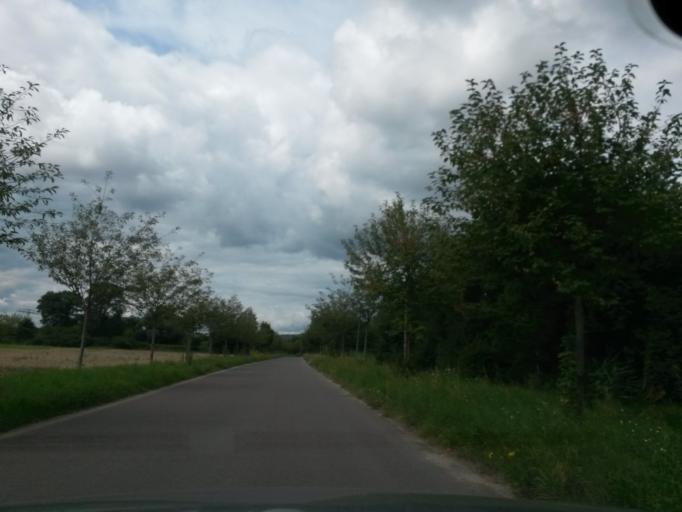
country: DE
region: Brandenburg
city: Oderberg
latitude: 52.8627
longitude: 14.0659
